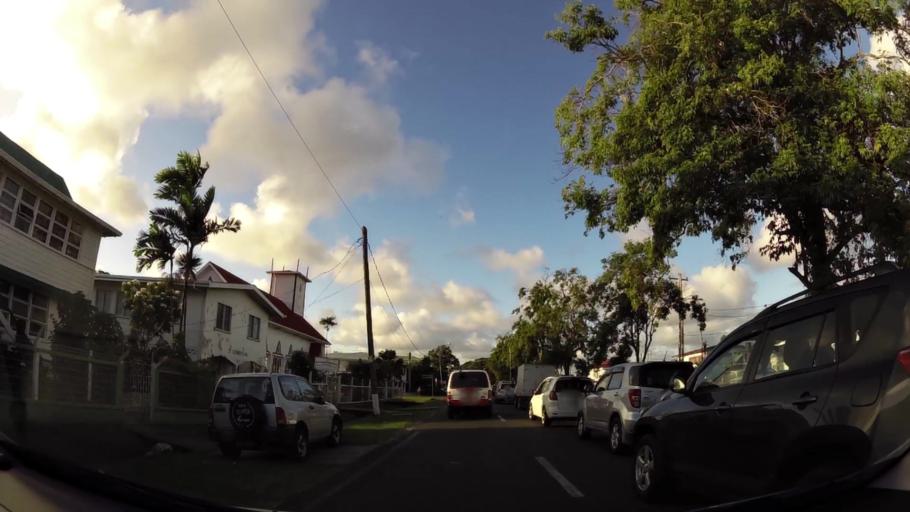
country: GY
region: Demerara-Mahaica
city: Georgetown
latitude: 6.8139
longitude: -58.1465
